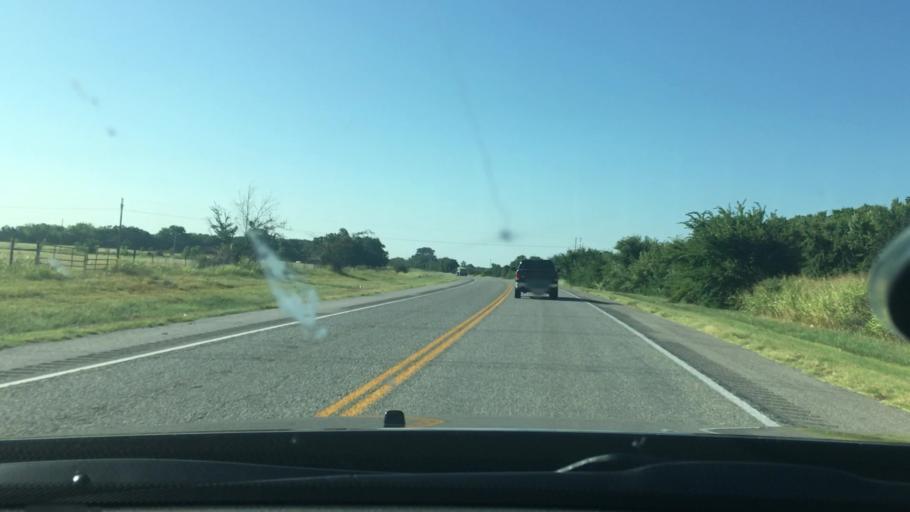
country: US
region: Oklahoma
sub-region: Johnston County
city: Tishomingo
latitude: 34.2640
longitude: -96.7715
